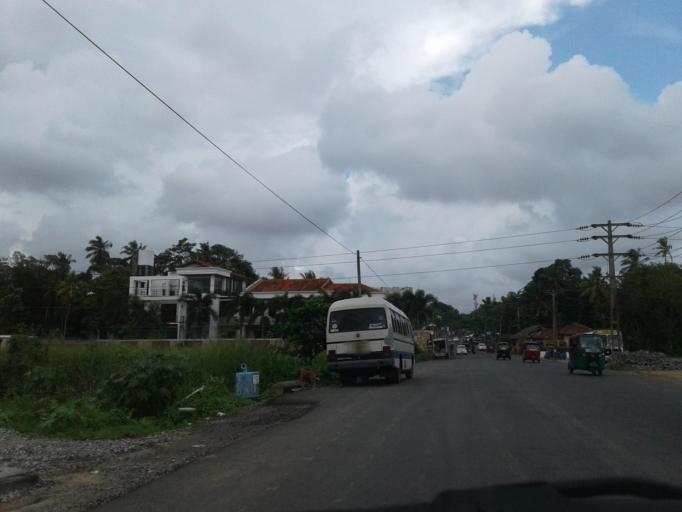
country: LK
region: Western
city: Moratuwa
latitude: 6.7967
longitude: 79.8943
